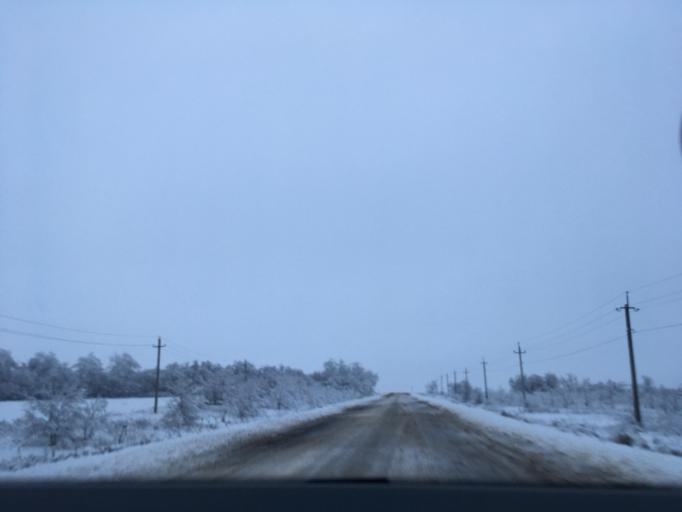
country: RU
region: Voronezj
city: Verkhniy Mamon
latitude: 50.0324
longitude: 40.0647
